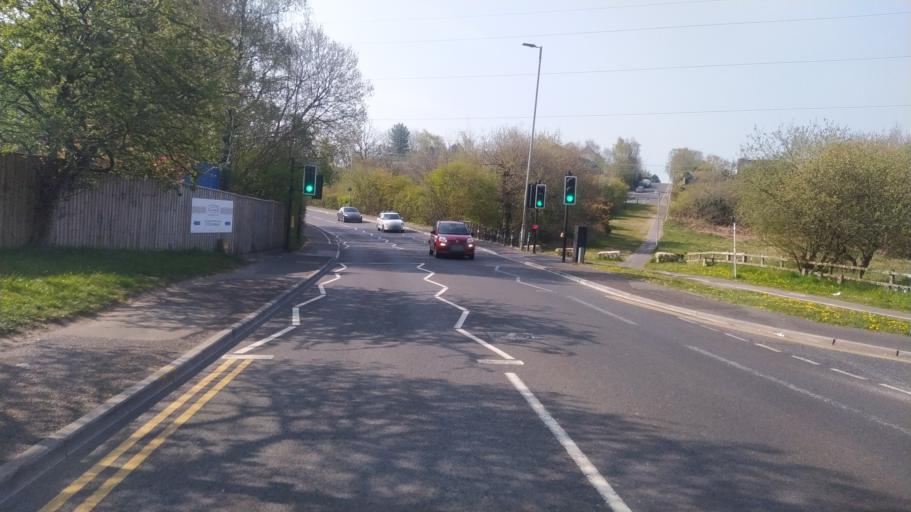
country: GB
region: England
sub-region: Dorset
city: Parkstone
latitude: 50.7425
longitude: -1.9120
